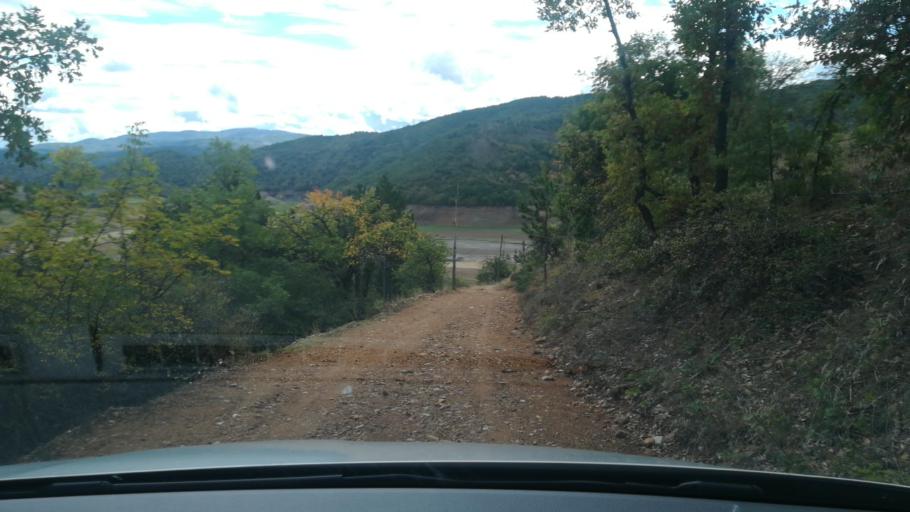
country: MK
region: Makedonska Kamenica
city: Makedonska Kamenica
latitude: 42.0040
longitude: 22.6064
